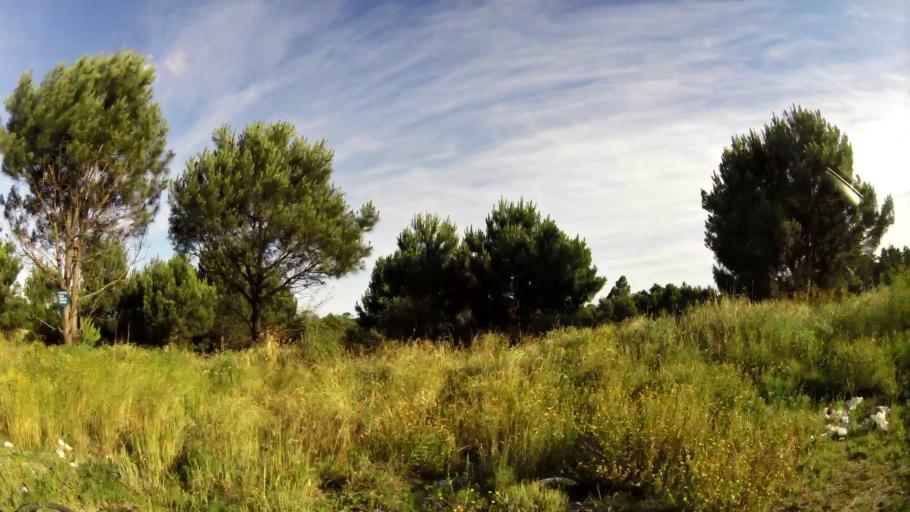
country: UY
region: Canelones
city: Empalme Olmos
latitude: -34.7645
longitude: -55.8575
